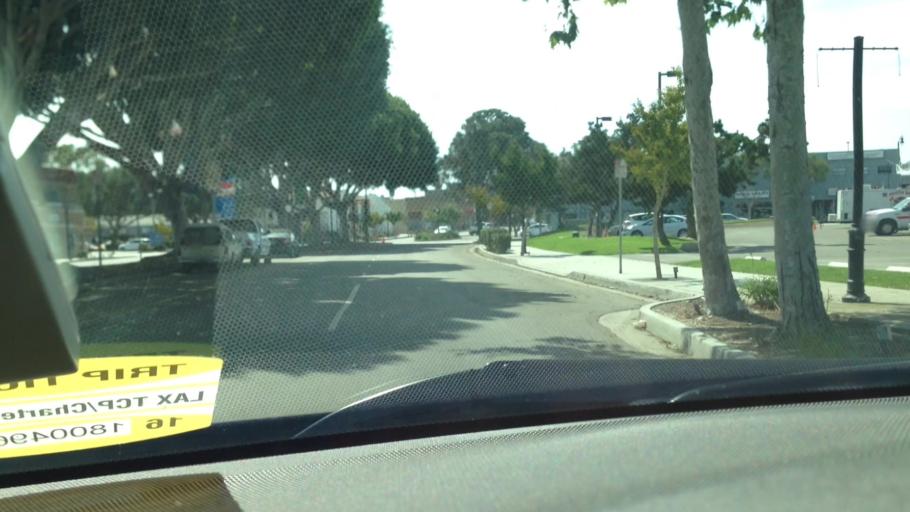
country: US
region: California
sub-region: Los Angeles County
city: El Segundo
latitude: 33.9193
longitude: -118.4148
